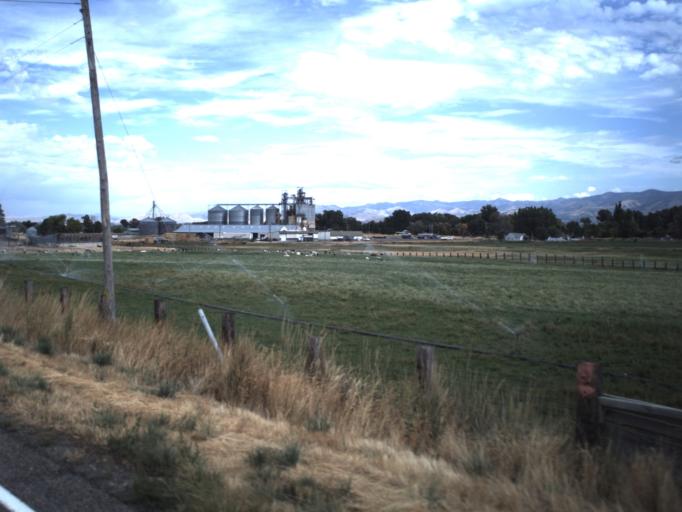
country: US
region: Utah
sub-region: Cache County
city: Lewiston
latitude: 41.9138
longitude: -111.9527
